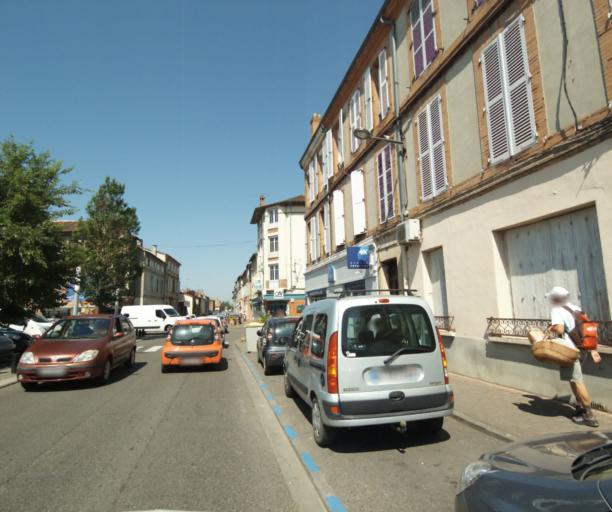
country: FR
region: Midi-Pyrenees
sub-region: Departement du Tarn-et-Garonne
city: Montauban
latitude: 44.0167
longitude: 1.3445
